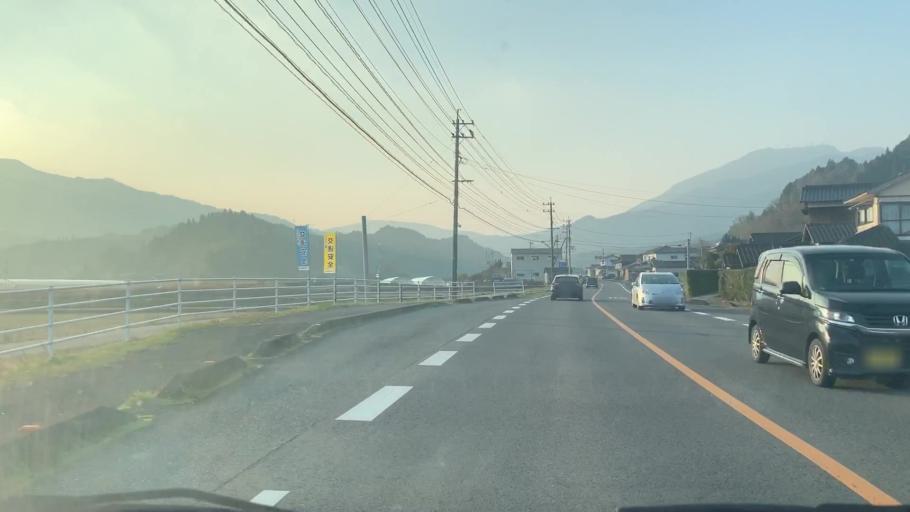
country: JP
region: Saga Prefecture
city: Takeocho-takeo
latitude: 33.2587
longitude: 130.0681
